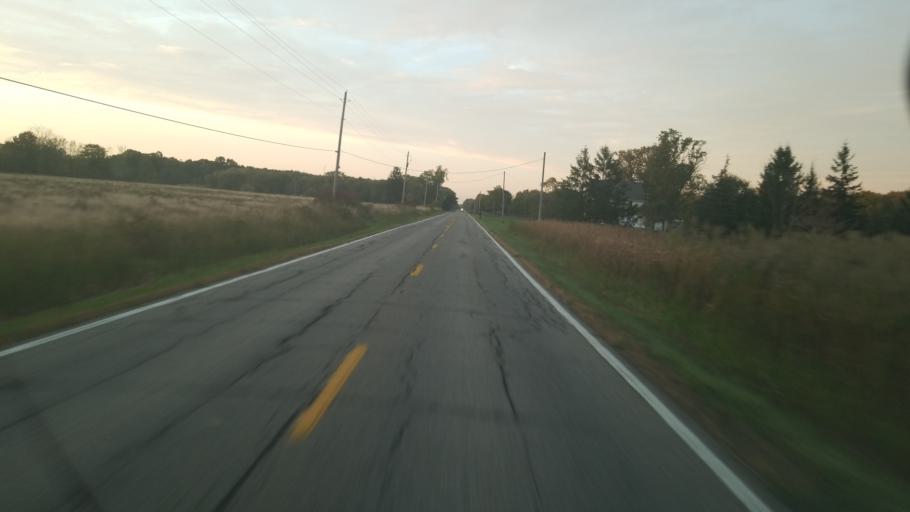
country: US
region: Ohio
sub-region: Ashtabula County
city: Andover
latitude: 41.6411
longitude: -80.6669
